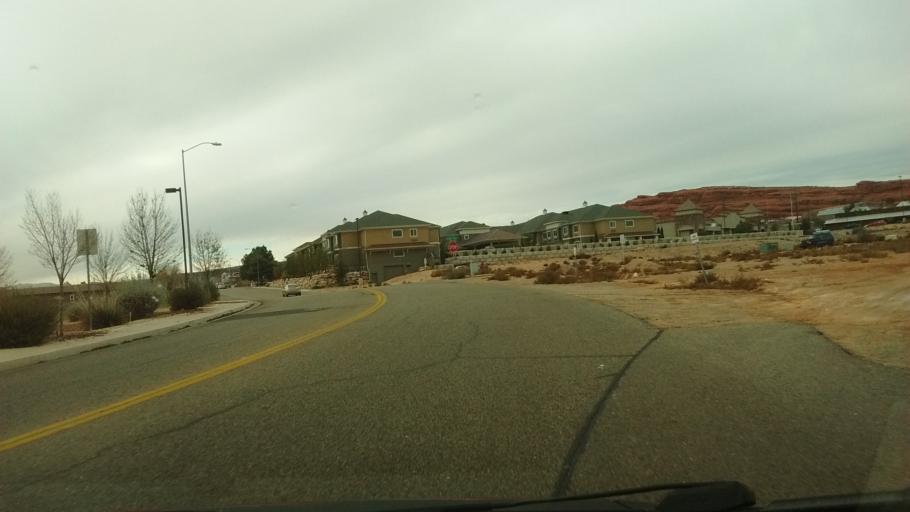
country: US
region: Utah
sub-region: Washington County
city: Washington
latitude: 37.1228
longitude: -113.5273
